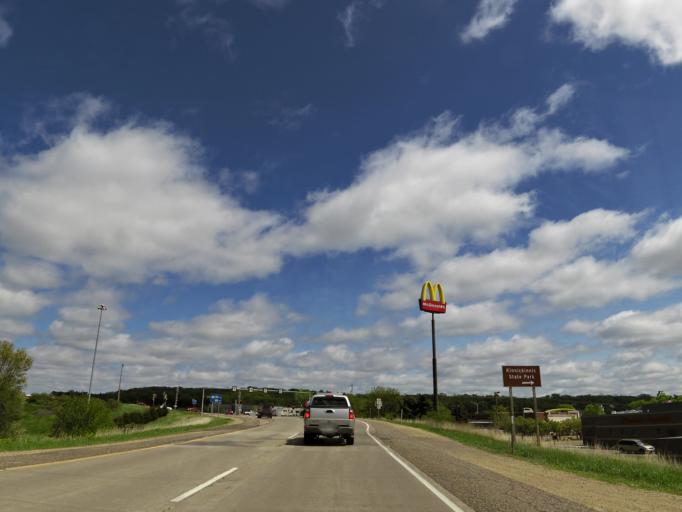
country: US
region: Wisconsin
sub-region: Saint Croix County
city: Hudson
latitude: 44.9624
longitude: -92.7235
